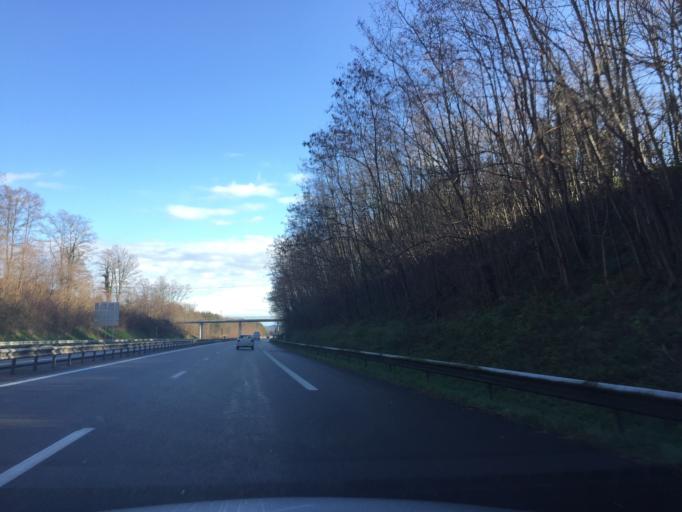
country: FR
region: Auvergne
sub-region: Departement du Puy-de-Dome
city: Lezoux
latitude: 45.8524
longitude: 3.3897
